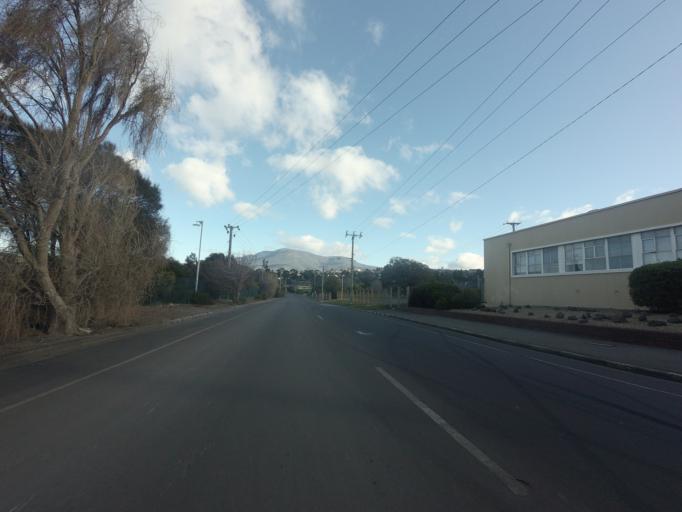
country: AU
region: Tasmania
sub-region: Glenorchy
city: Lutana
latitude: -42.8375
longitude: 147.3202
